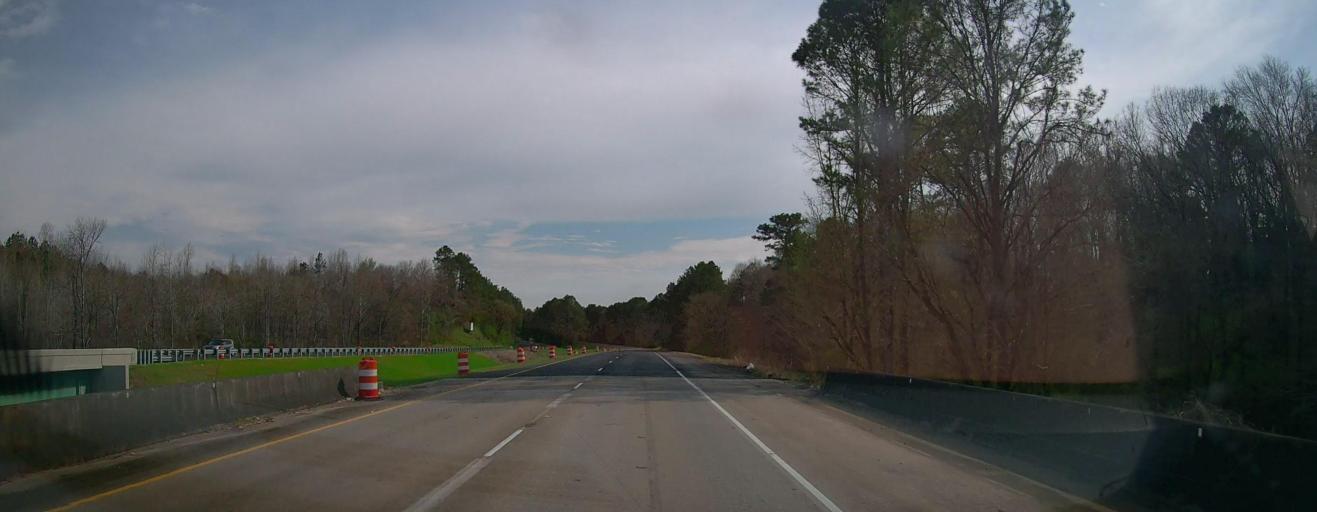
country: US
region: Alabama
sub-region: Walker County
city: Sumiton
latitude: 33.7046
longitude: -86.9922
